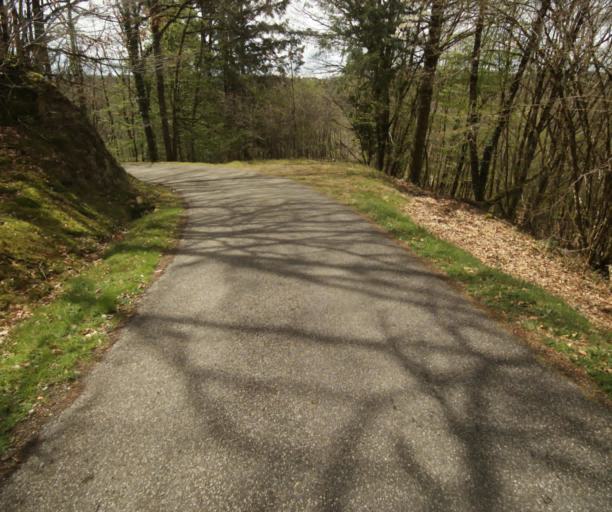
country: FR
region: Limousin
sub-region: Departement de la Correze
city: Sainte-Fortunade
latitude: 45.1935
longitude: 1.8760
